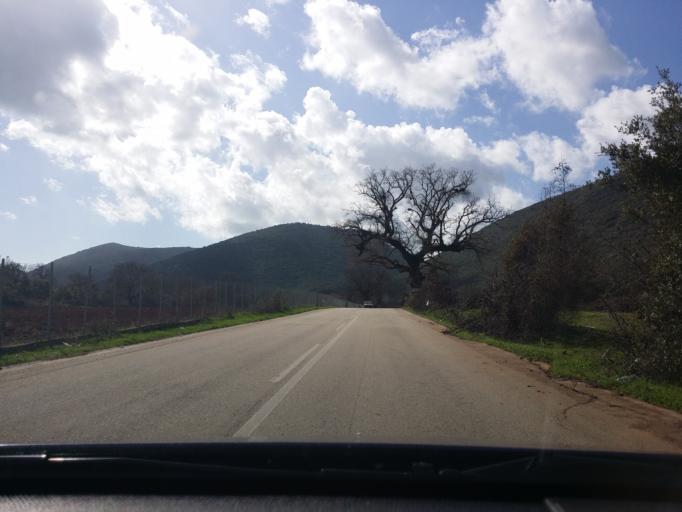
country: GR
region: West Greece
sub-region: Nomos Aitolias kai Akarnanias
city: Fitiai
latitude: 38.6200
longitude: 21.1465
